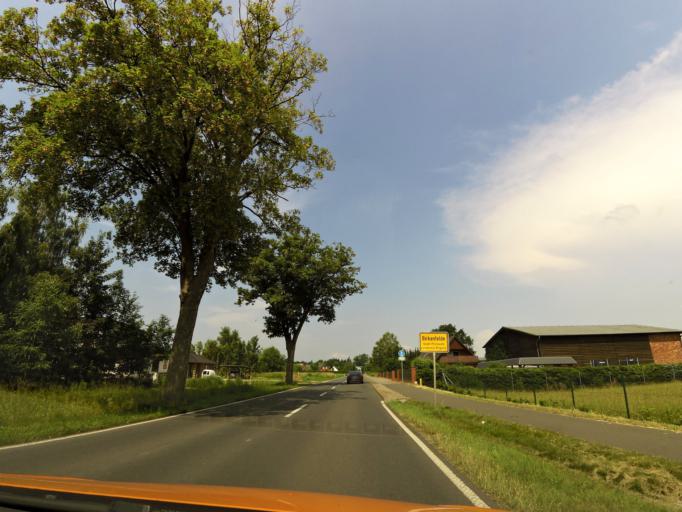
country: DE
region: Brandenburg
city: Pritzwalk
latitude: 53.1886
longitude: 12.1956
